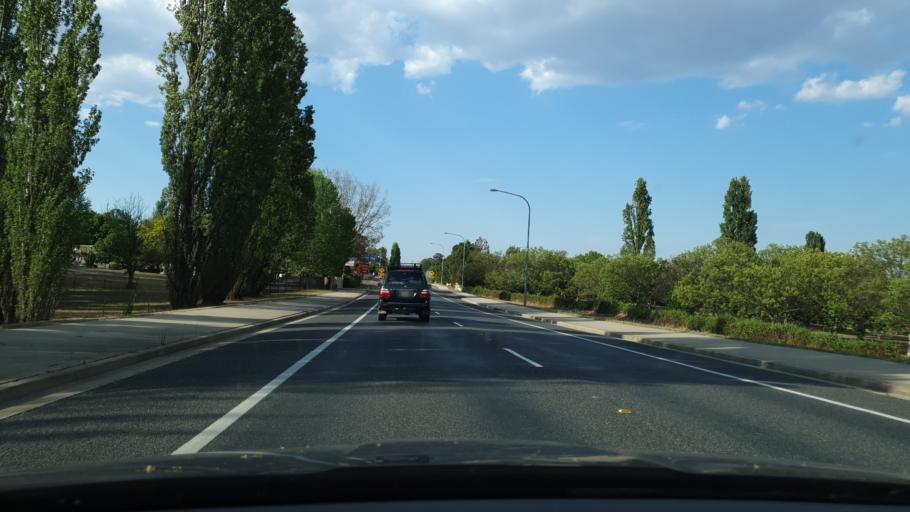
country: AU
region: New South Wales
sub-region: Tenterfield Municipality
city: Carrolls Creek
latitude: -29.0438
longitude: 152.0209
